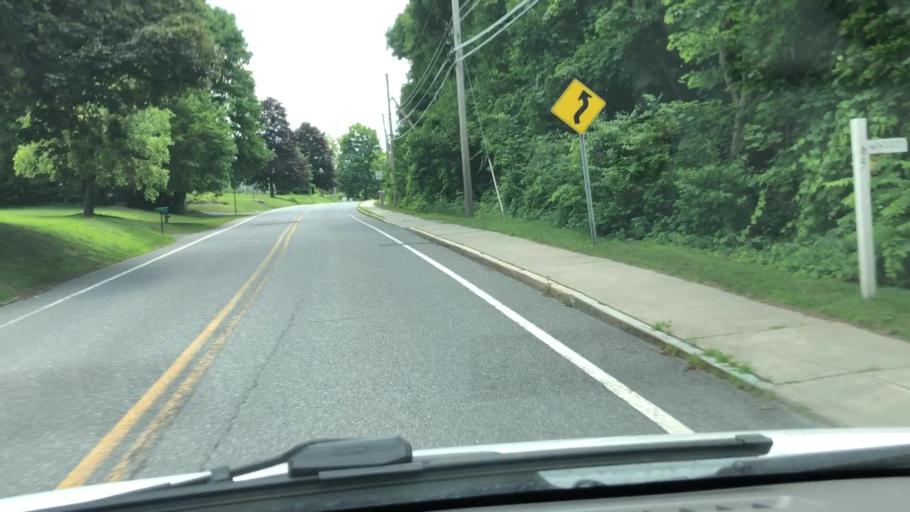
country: US
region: Massachusetts
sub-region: Berkshire County
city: Adams
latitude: 42.6122
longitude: -73.1185
